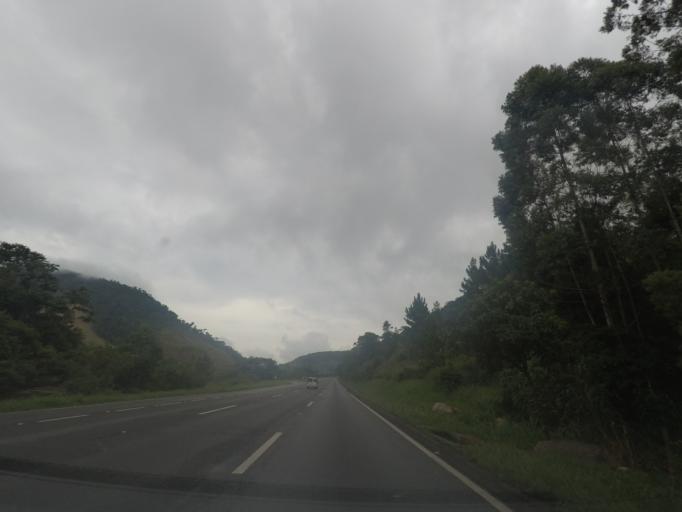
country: BR
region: Sao Paulo
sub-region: Cajati
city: Cajati
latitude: -24.8910
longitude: -48.2362
